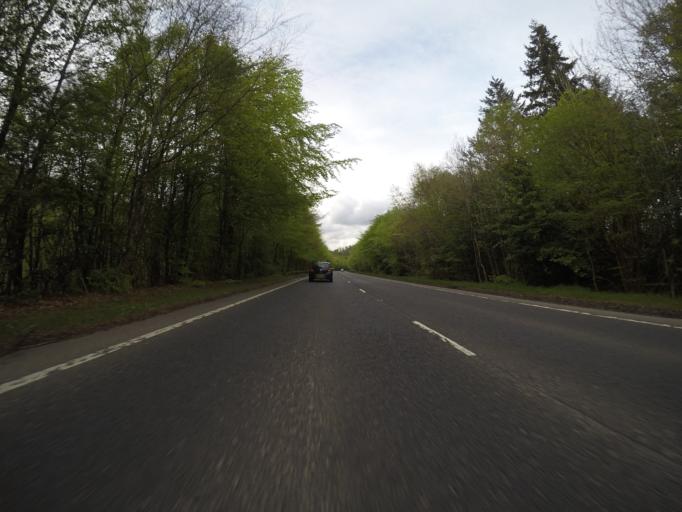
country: GB
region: Scotland
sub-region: West Dunbartonshire
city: Balloch
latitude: 56.0638
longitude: -4.6459
